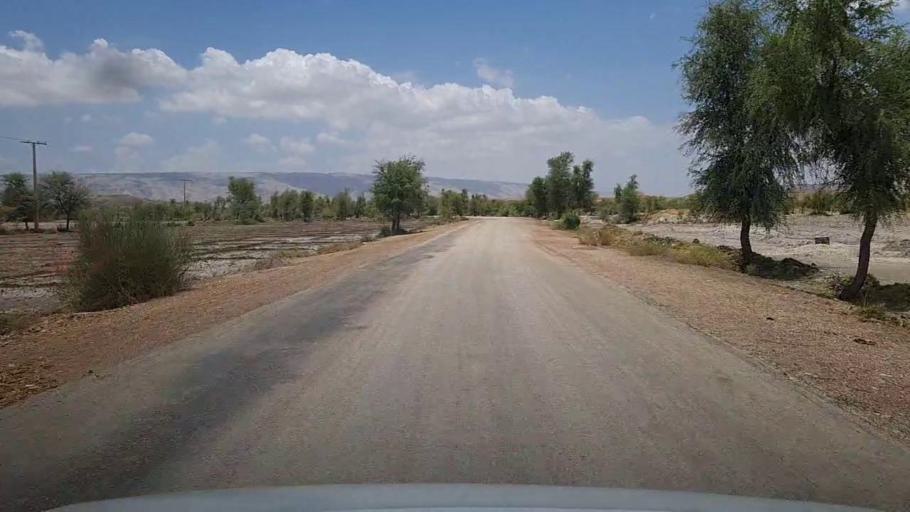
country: PK
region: Sindh
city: Bhan
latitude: 26.3163
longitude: 67.5801
